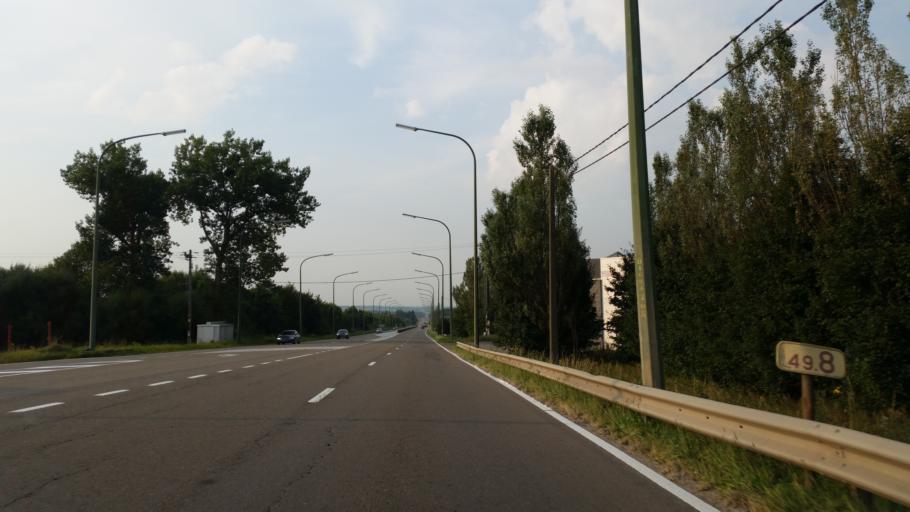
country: BE
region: Wallonia
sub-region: Province du Luxembourg
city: Marche-en-Famenne
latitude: 50.2421
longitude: 5.3452
